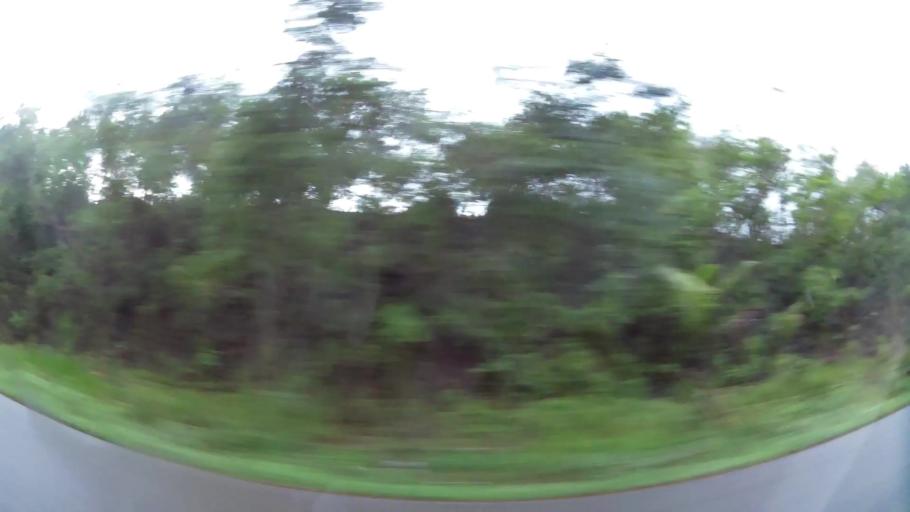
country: DO
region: San Cristobal
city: Villa Altagracia
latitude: 18.6006
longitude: -70.1345
